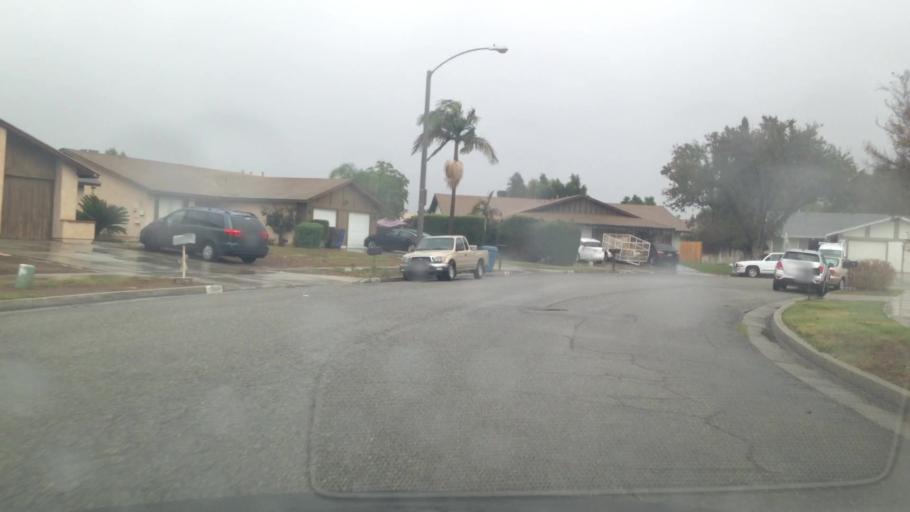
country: US
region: California
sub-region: Riverside County
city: Pedley
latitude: 33.9499
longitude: -117.4593
